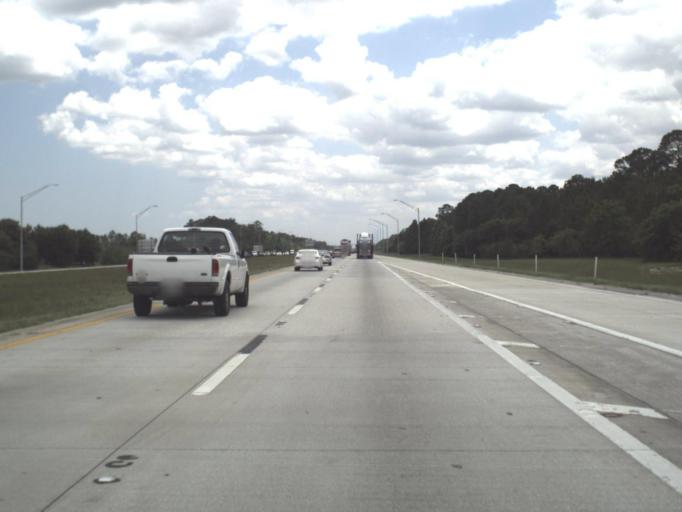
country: US
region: Florida
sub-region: Saint Johns County
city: Palm Valley
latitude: 30.2114
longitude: -81.5141
